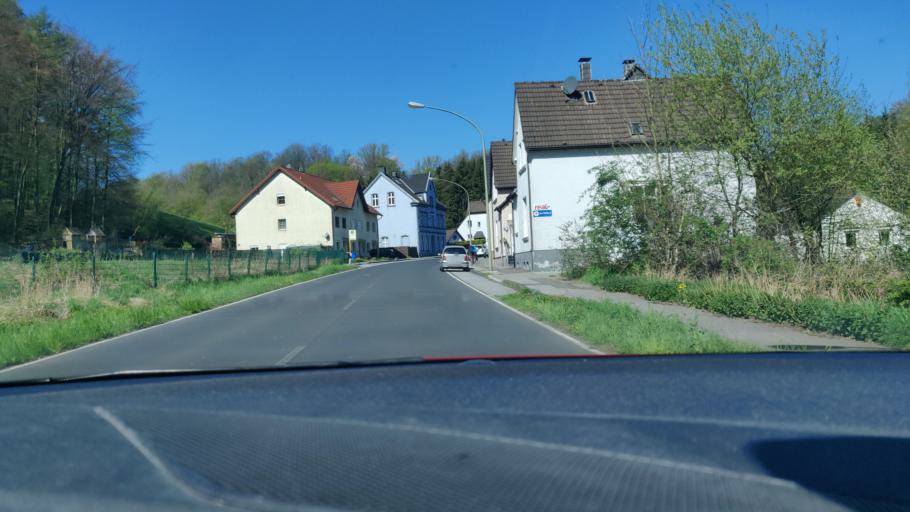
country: DE
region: North Rhine-Westphalia
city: Wulfrath
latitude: 51.2869
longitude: 7.0653
